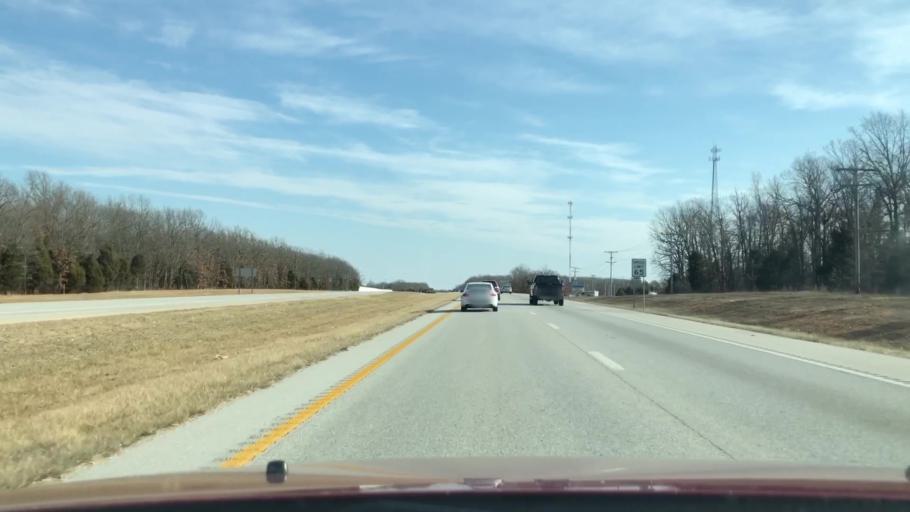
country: US
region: Missouri
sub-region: Webster County
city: Rogersville
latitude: 37.1168
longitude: -93.0222
